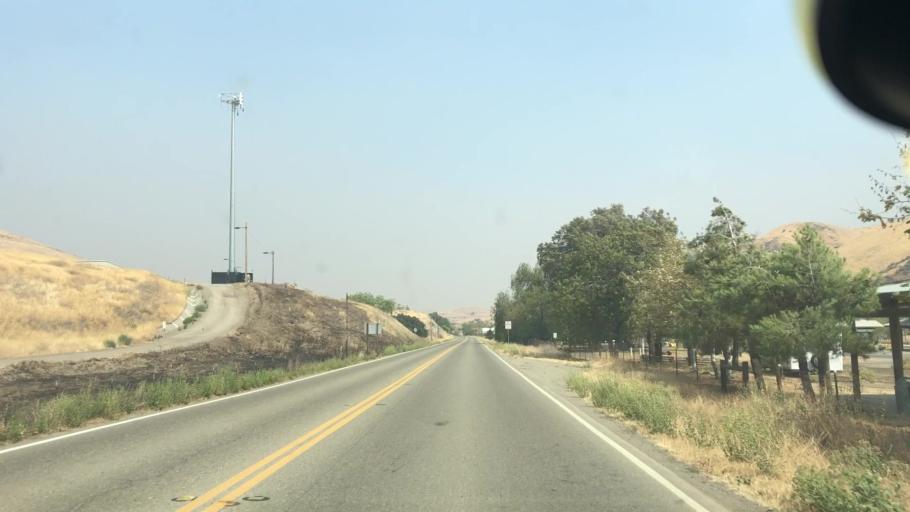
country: US
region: California
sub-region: San Joaquin County
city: Mountain House
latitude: 37.6340
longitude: -121.5438
